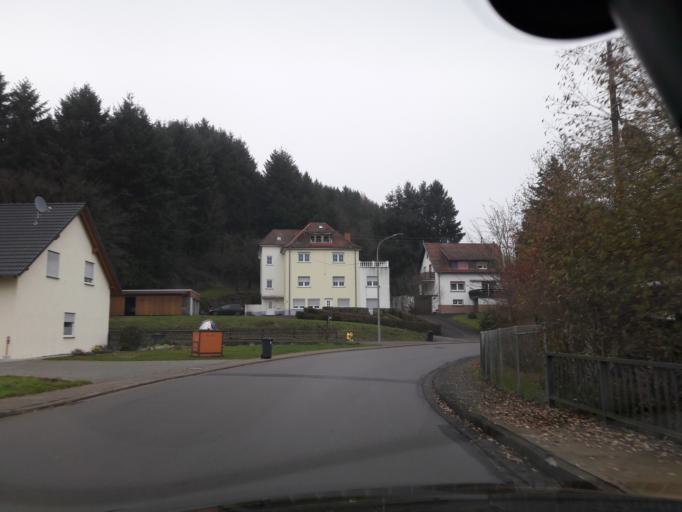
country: DE
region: Rheinland-Pfalz
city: Krottelbach
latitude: 49.4705
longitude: 7.3458
